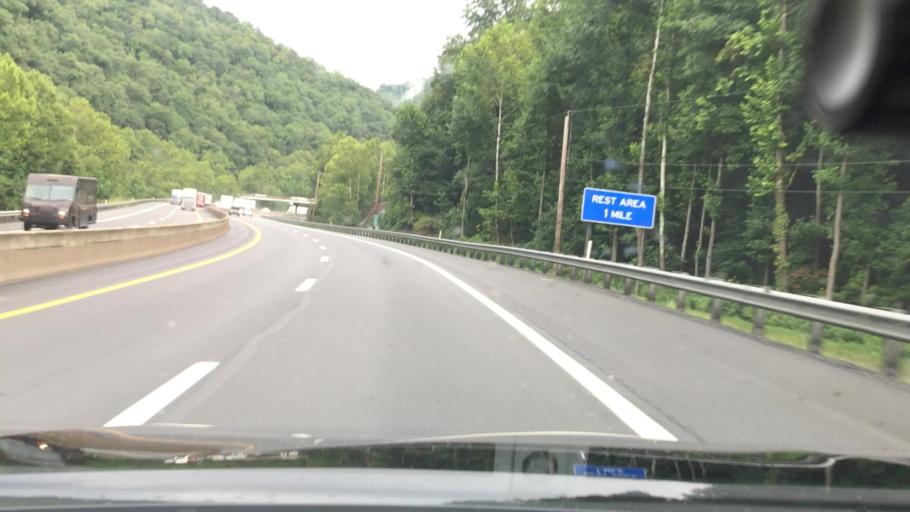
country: US
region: West Virginia
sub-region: Kanawha County
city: Montgomery
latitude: 38.0843
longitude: -81.3859
